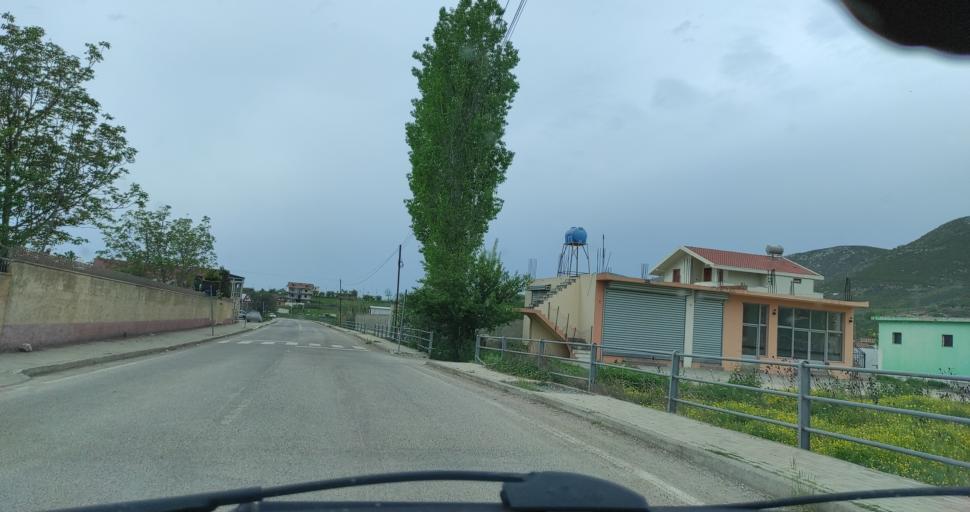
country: AL
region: Lezhe
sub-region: Rrethi i Kurbinit
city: Lac
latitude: 41.6091
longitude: 19.7136
